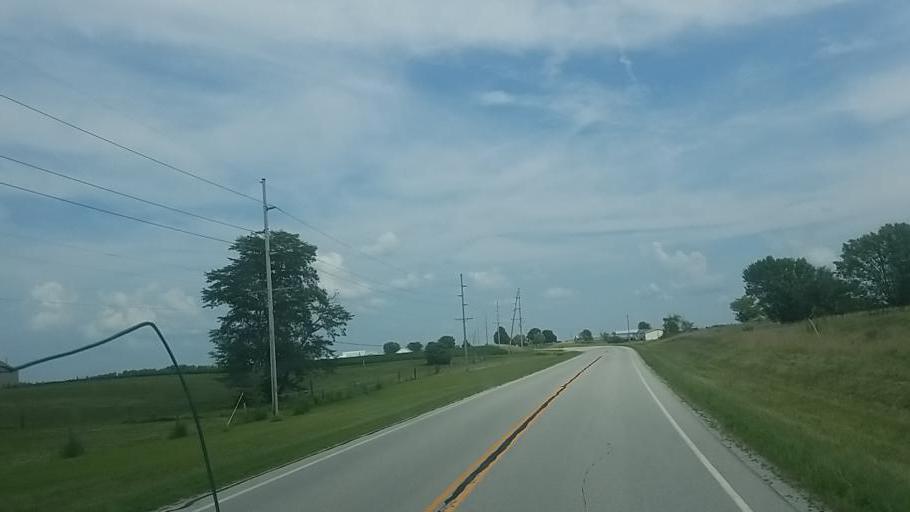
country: US
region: Ohio
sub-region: Hardin County
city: Forest
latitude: 40.7824
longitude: -83.5690
